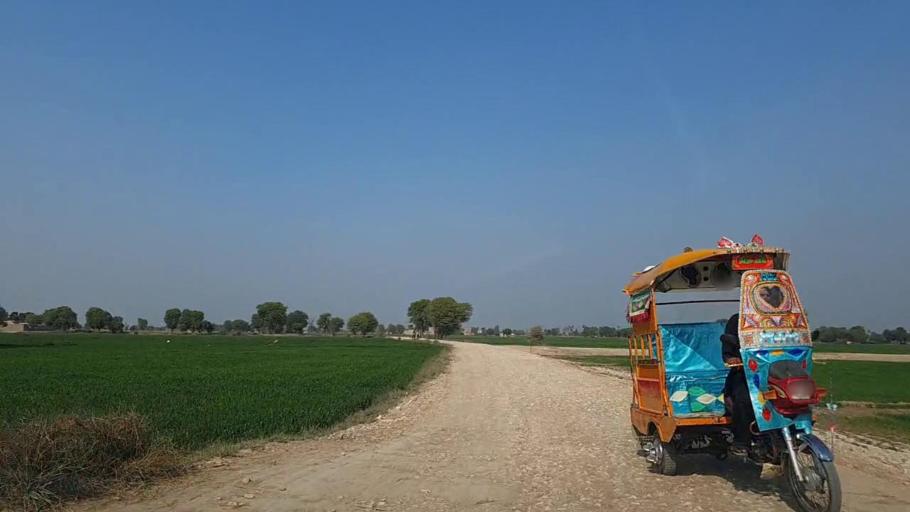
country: PK
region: Sindh
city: Moro
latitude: 26.6951
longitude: 67.9513
